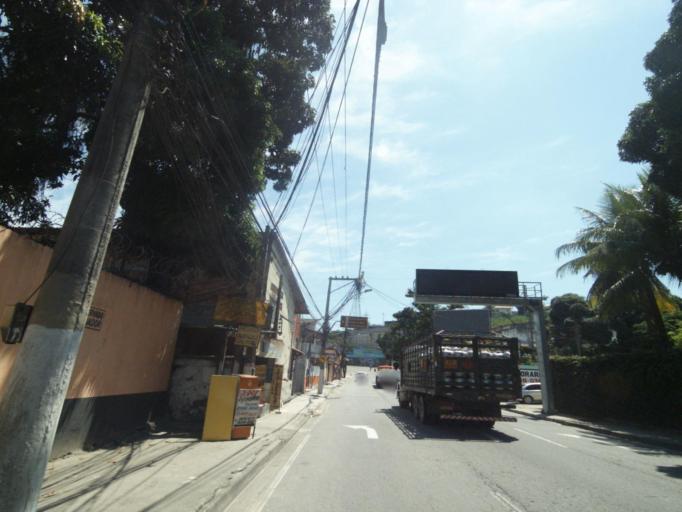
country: BR
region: Rio de Janeiro
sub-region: Niteroi
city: Niteroi
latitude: -22.9059
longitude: -43.0643
